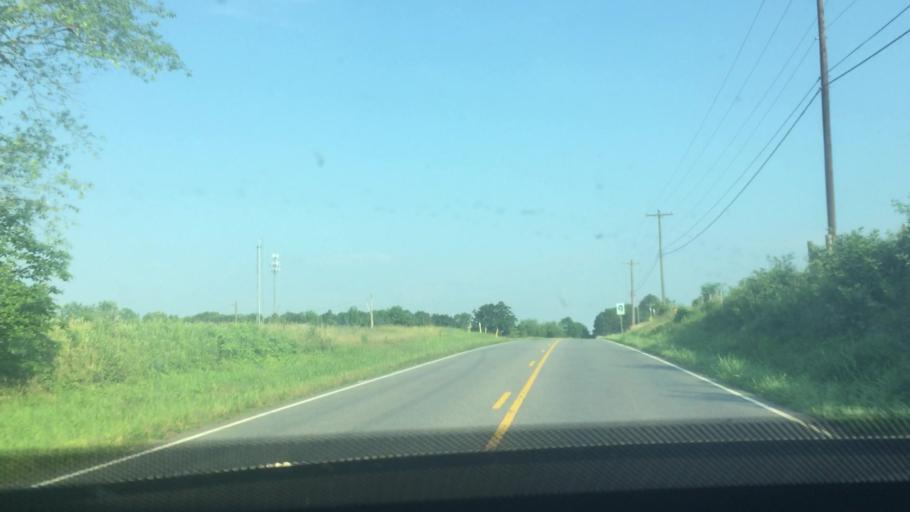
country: US
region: North Carolina
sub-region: Iredell County
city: Mooresville
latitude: 35.5916
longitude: -80.7555
